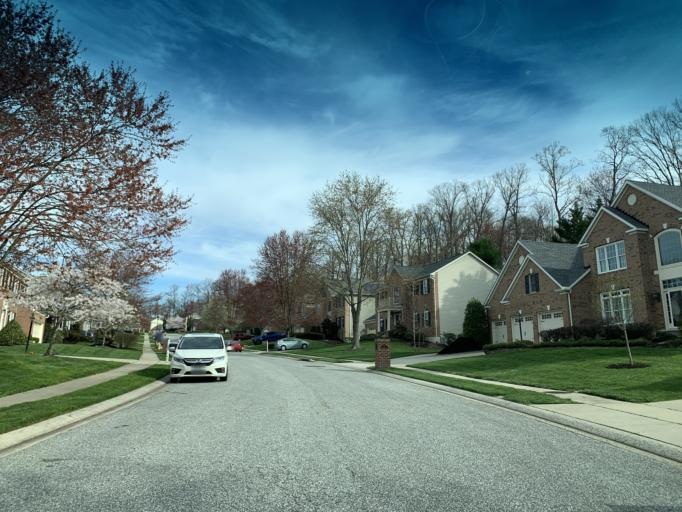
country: US
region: Maryland
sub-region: Harford County
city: South Bel Air
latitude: 39.5664
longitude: -76.3347
